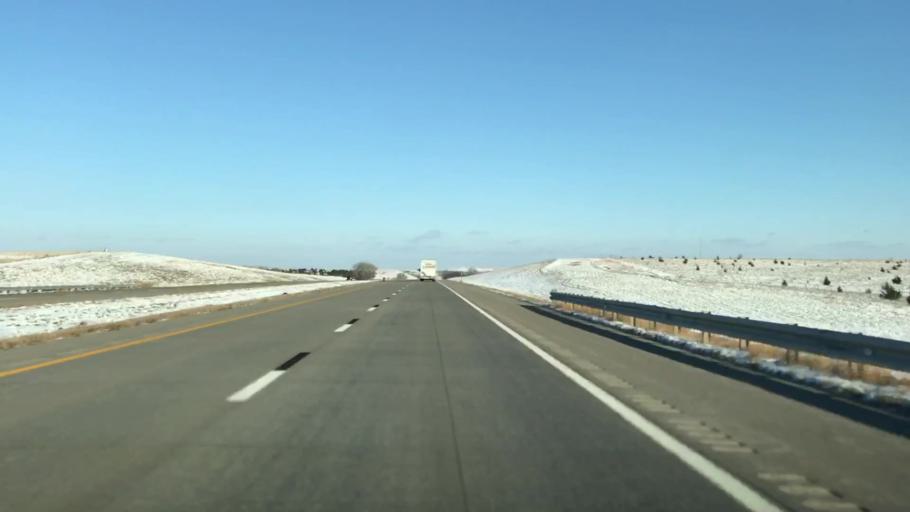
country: US
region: Kansas
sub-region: Lincoln County
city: Lincoln
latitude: 38.8781
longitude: -97.9544
